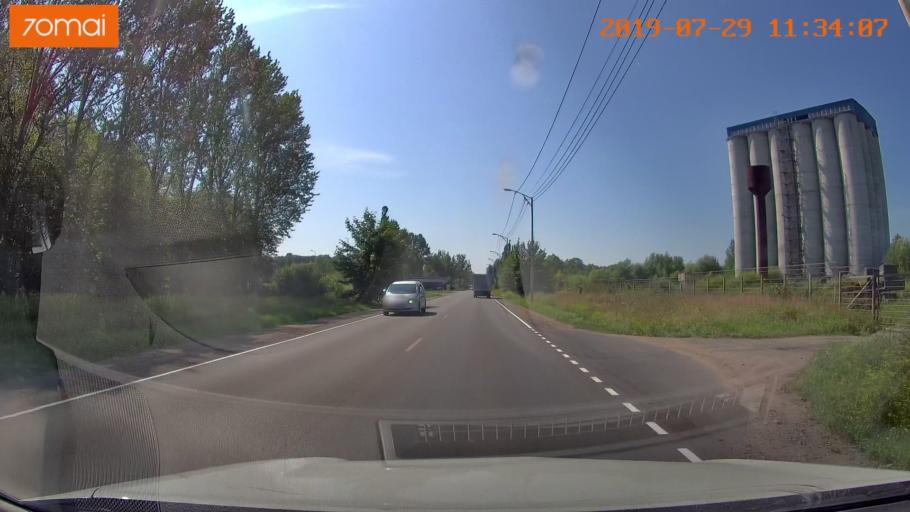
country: RU
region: Kaliningrad
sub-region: Gorod Kaliningrad
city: Kaliningrad
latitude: 54.6585
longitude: 20.5416
